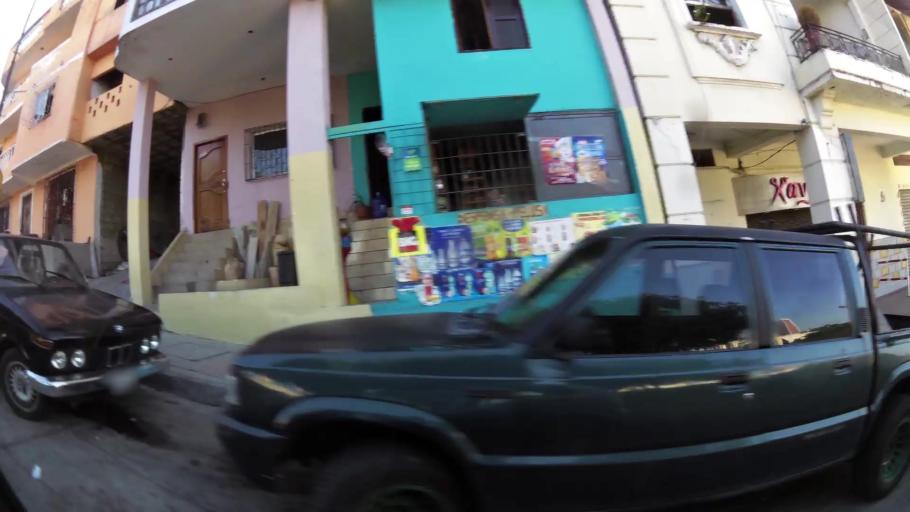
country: EC
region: Guayas
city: Eloy Alfaro
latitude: -2.1824
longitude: -79.8769
